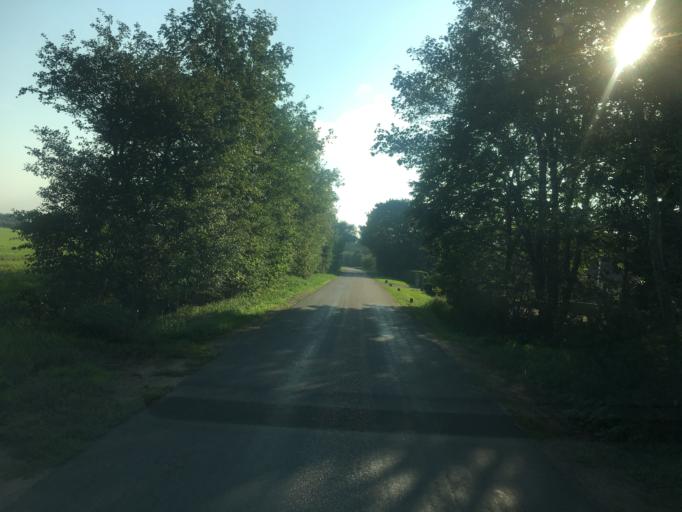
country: DE
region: Schleswig-Holstein
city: Bramstedtlund
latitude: 54.9303
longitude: 9.0623
